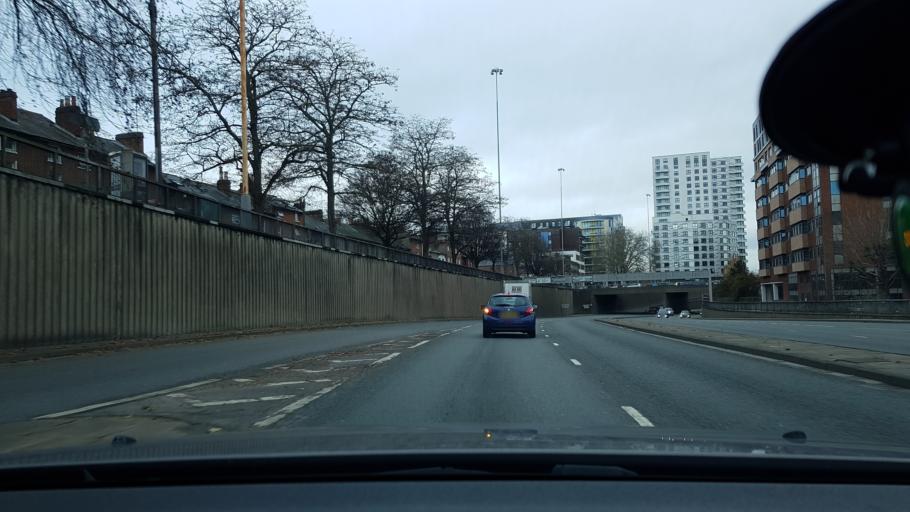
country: GB
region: England
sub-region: Reading
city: Reading
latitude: 51.4532
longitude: -0.9784
